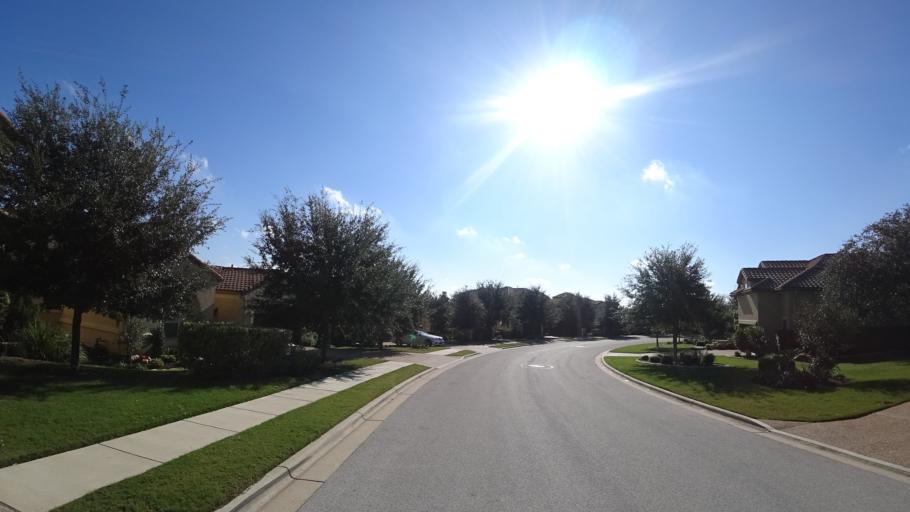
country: US
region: Texas
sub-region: Travis County
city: Bee Cave
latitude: 30.3486
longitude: -97.8932
